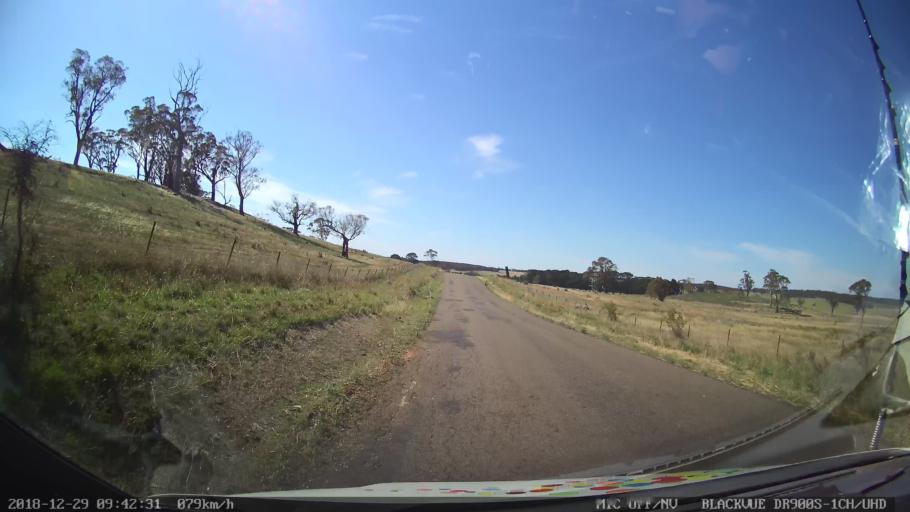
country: AU
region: New South Wales
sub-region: Upper Lachlan Shire
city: Crookwell
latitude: -34.6706
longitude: 149.4207
